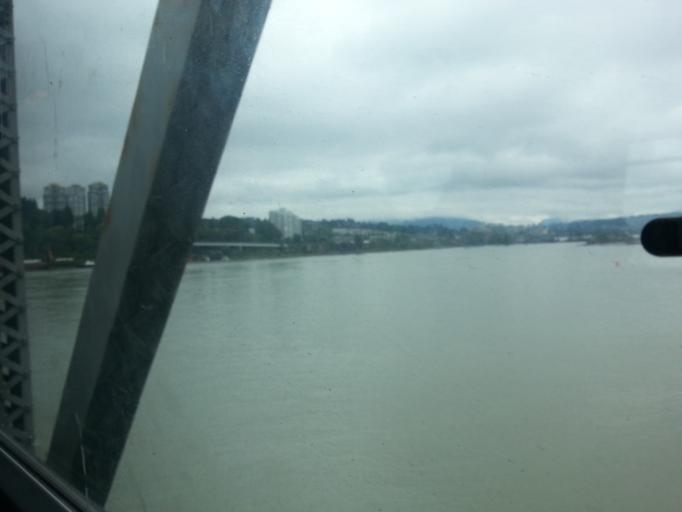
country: CA
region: British Columbia
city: New Westminster
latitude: 49.2072
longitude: -122.8911
